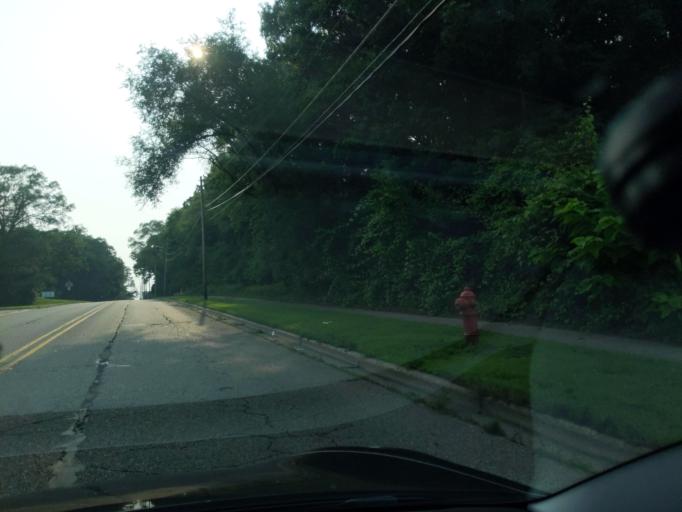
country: US
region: Michigan
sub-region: Jackson County
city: Jackson
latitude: 42.2620
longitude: -84.4296
